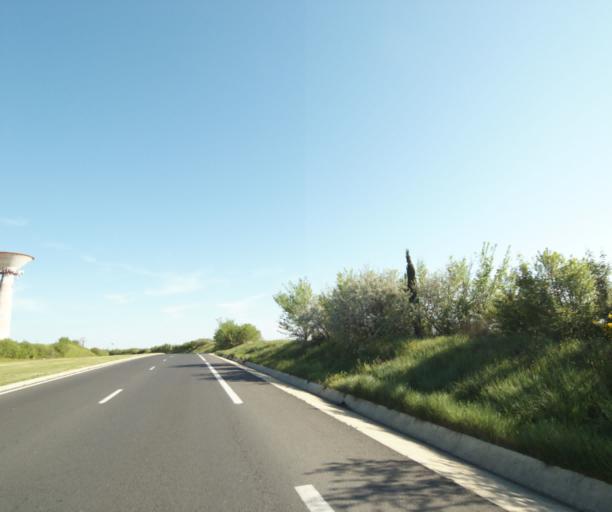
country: FR
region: Languedoc-Roussillon
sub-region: Departement de l'Herault
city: Le Cres
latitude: 43.6312
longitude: 3.9355
